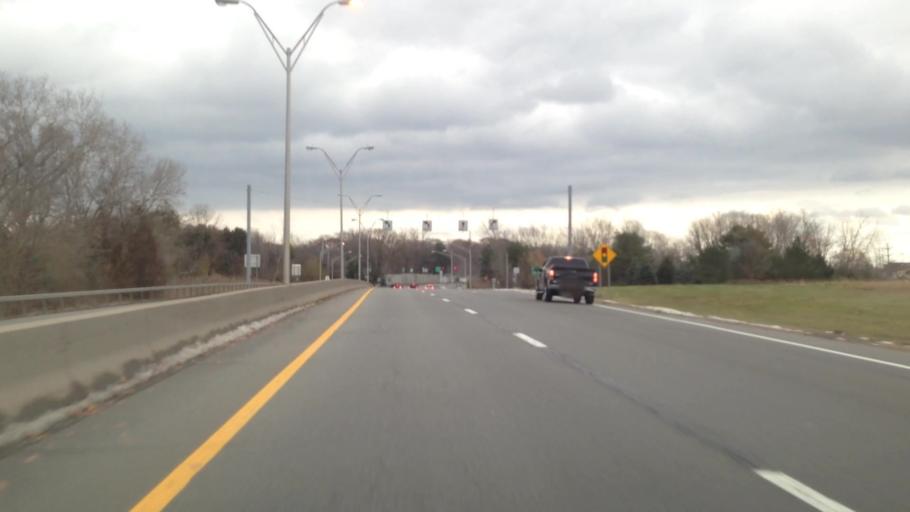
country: US
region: New York
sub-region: Monroe County
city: North Gates
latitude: 43.1273
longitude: -77.7046
